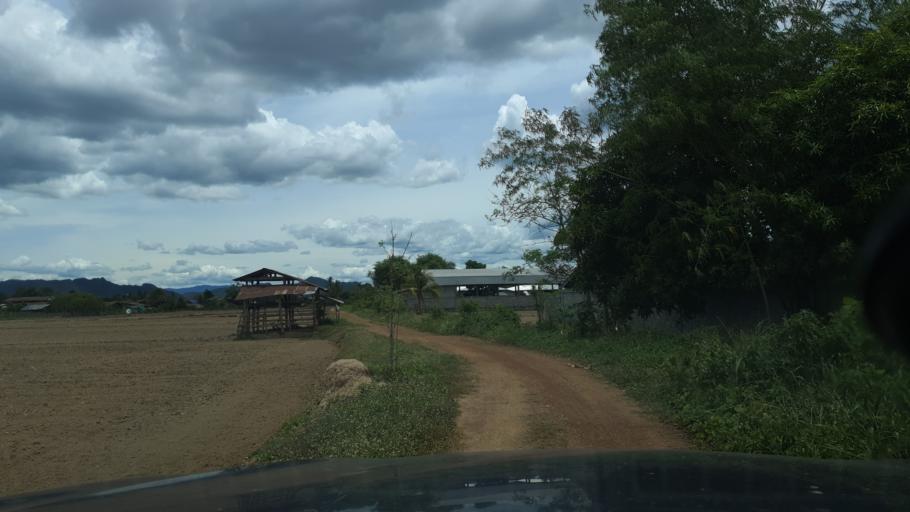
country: TH
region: Sukhothai
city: Thung Saliam
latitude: 17.3128
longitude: 99.5699
